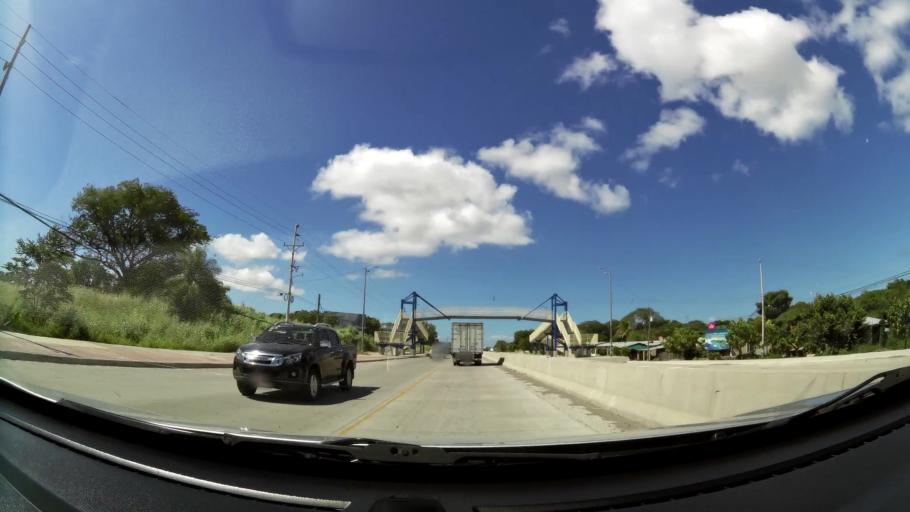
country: CR
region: Guanacaste
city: Bagaces
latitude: 10.5196
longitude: -85.2486
